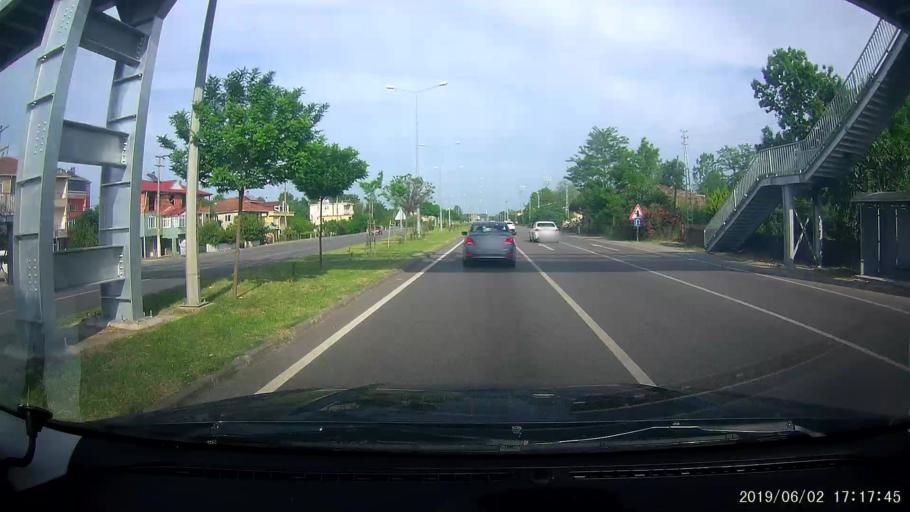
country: TR
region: Samsun
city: Dikbiyik
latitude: 41.2271
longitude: 36.5867
